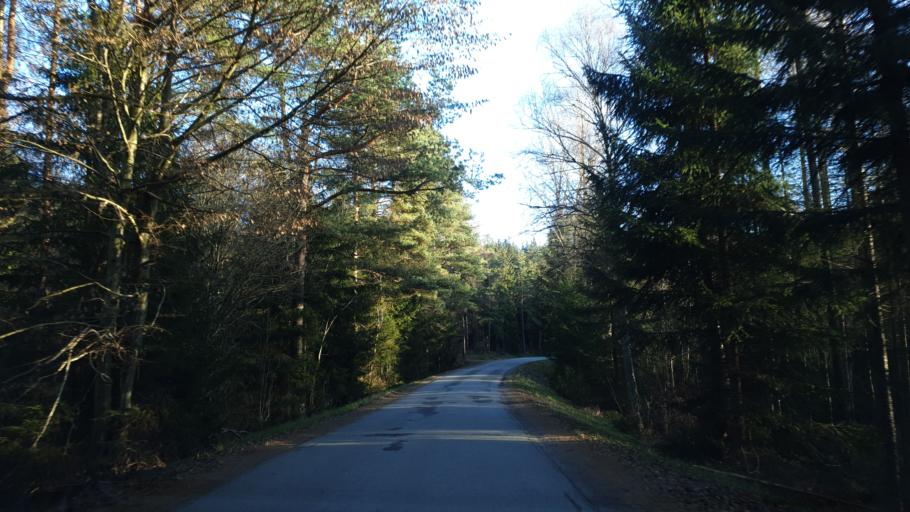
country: SE
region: Blekinge
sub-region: Ronneby Kommun
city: Brakne-Hoby
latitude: 56.2313
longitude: 15.1612
